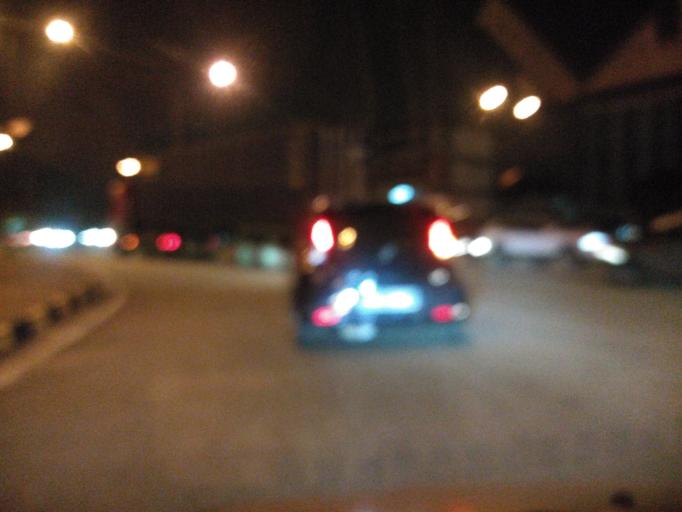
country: MY
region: Penang
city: Butterworth
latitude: 5.4072
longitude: 100.3701
